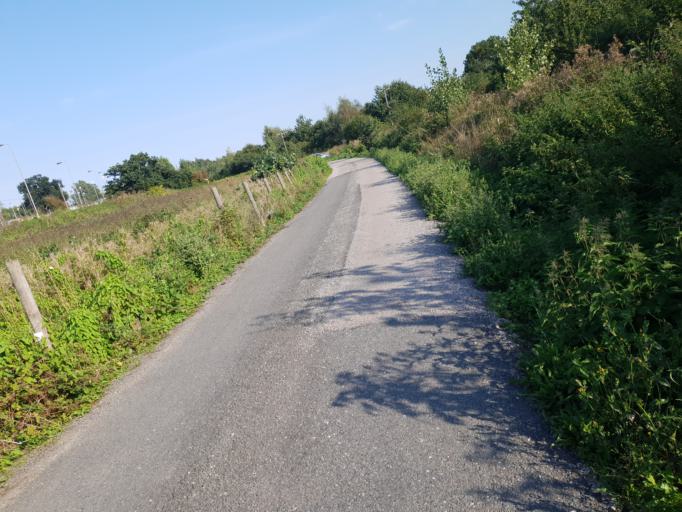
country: GB
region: England
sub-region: Essex
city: Manningtree
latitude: 51.9486
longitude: 1.0421
